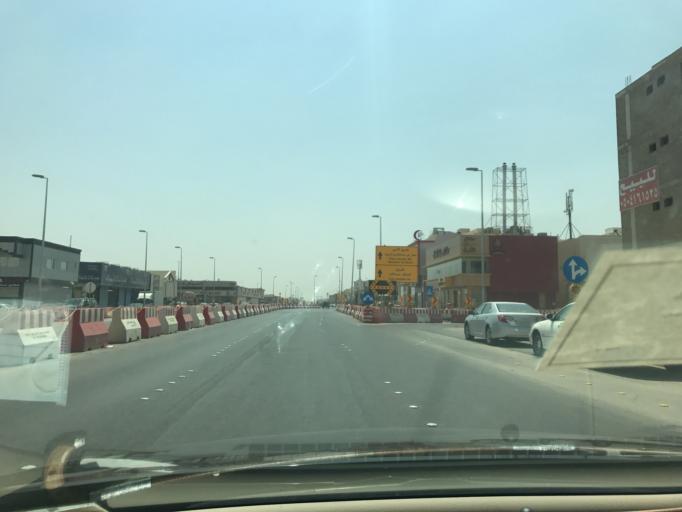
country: SA
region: Ar Riyad
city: Riyadh
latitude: 24.7485
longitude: 46.7734
